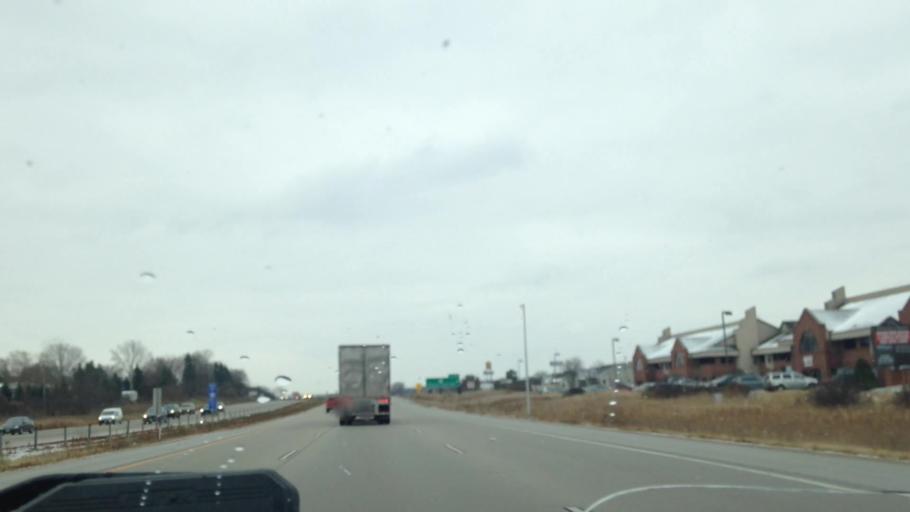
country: US
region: Wisconsin
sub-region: Waukesha County
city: Menomonee Falls
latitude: 43.1980
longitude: -88.1304
